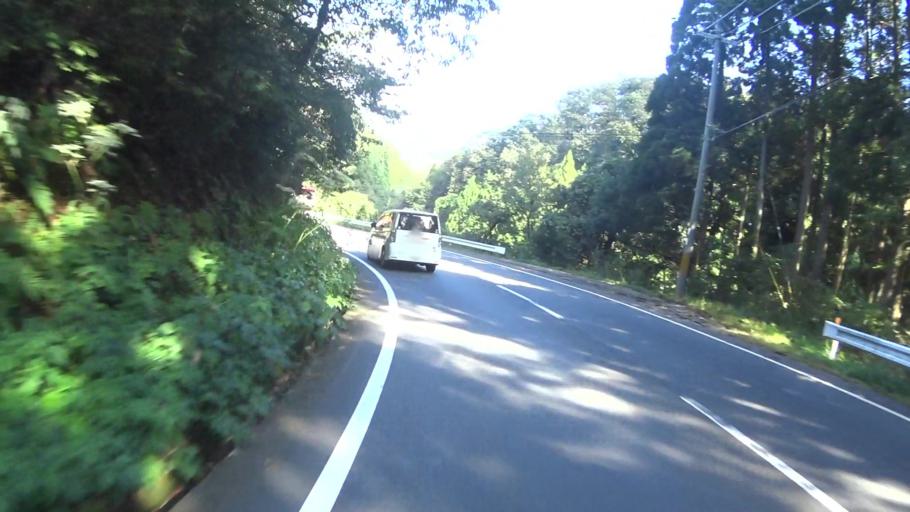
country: JP
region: Kyoto
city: Miyazu
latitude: 35.6405
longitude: 135.1304
